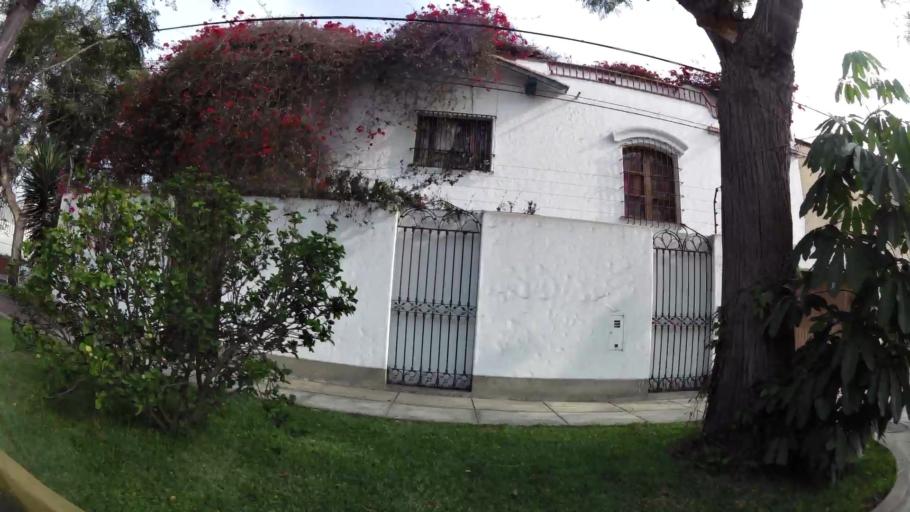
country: PE
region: Lima
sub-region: Lima
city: San Isidro
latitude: -12.0938
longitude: -77.0549
